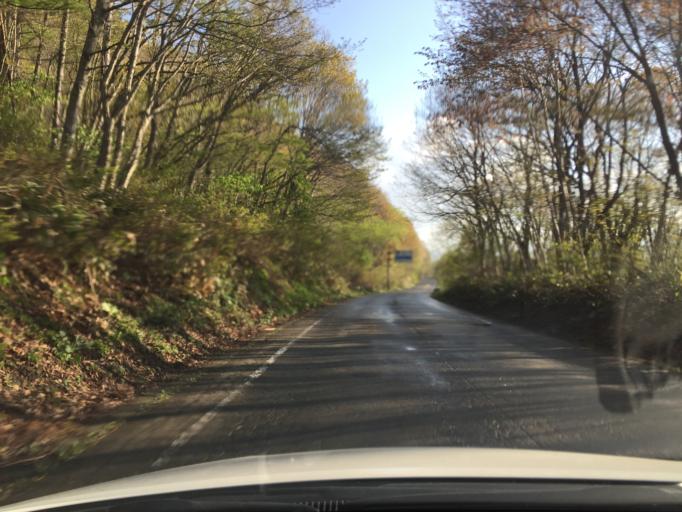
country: JP
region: Fukushima
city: Inawashiro
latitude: 37.6519
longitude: 140.0385
